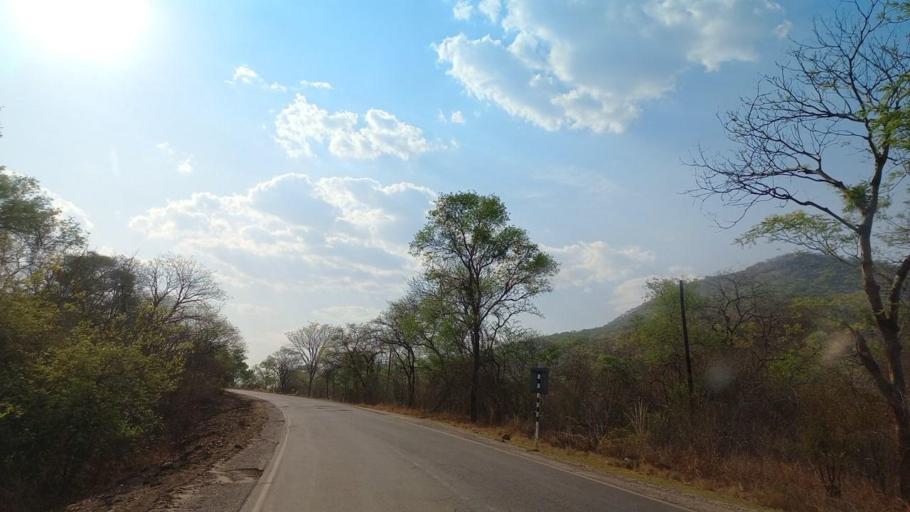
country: ZM
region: Lusaka
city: Luangwa
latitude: -14.9813
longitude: 30.1487
